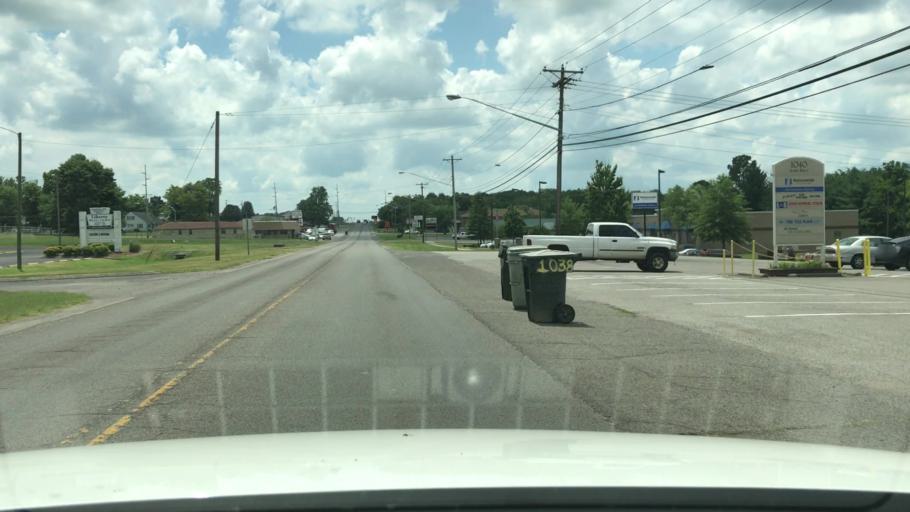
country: US
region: Tennessee
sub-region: Sumner County
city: Gallatin
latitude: 36.3704
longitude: -86.4409
